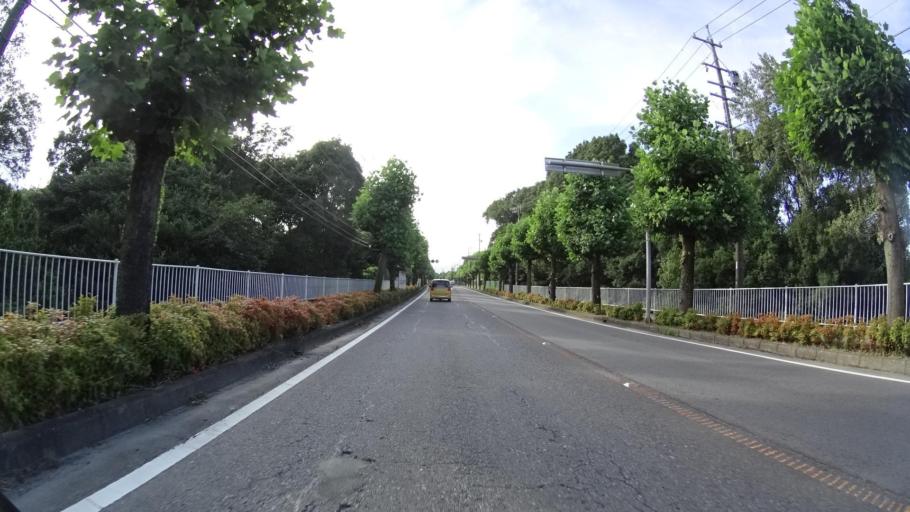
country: JP
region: Mie
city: Kawage
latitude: 34.8487
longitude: 136.5374
